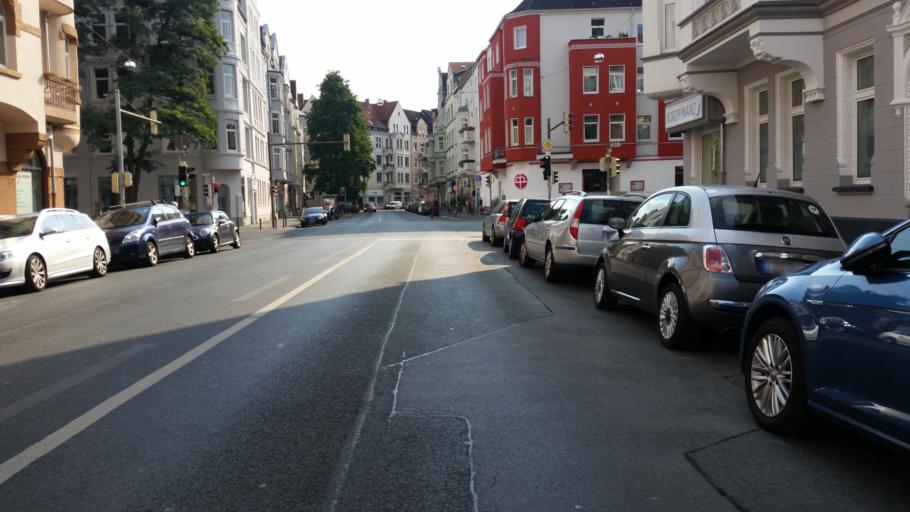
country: DE
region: Lower Saxony
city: Hannover
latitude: 52.3909
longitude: 9.7443
